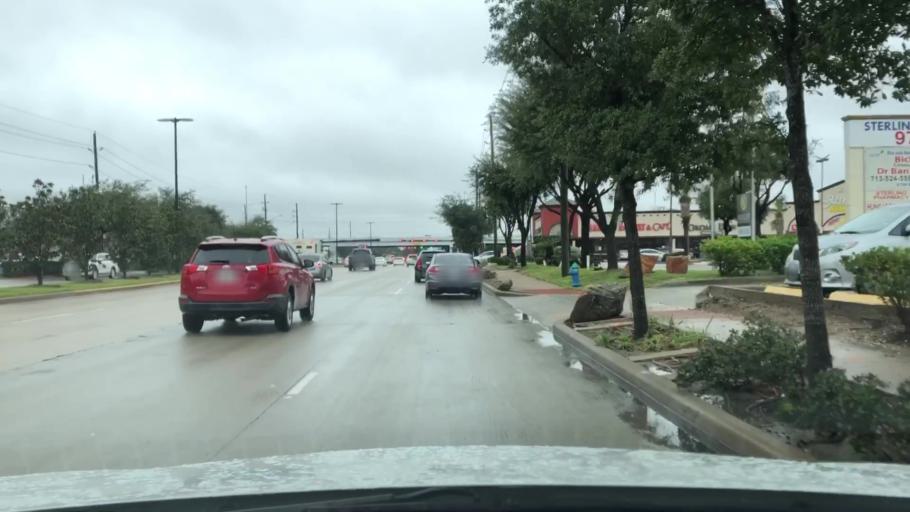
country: US
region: Texas
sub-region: Fort Bend County
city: Meadows Place
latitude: 29.7048
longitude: -95.5544
